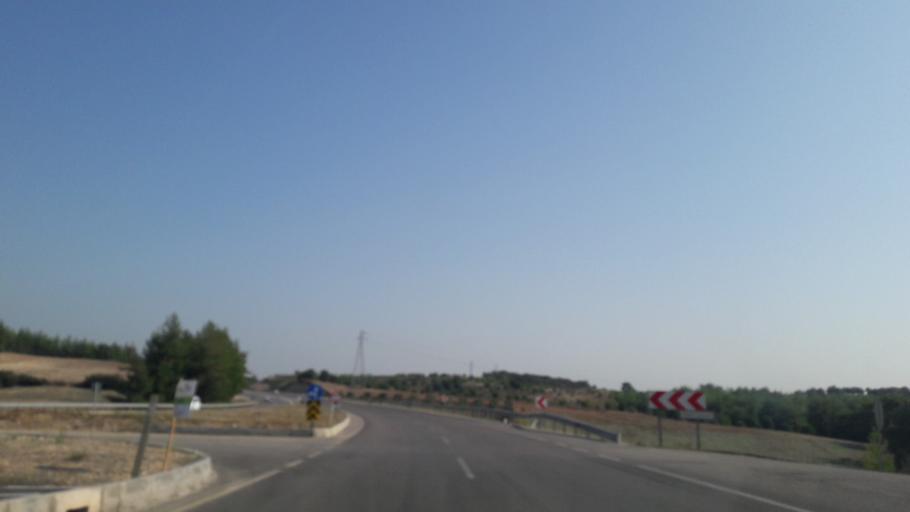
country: TR
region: Adana
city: Sagkaya
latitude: 37.1605
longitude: 35.5549
